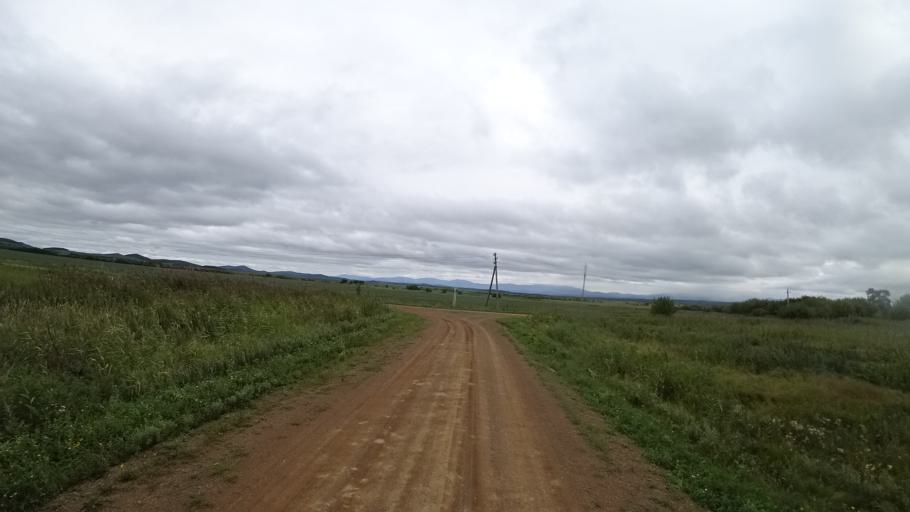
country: RU
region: Primorskiy
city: Chernigovka
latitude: 44.4351
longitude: 132.5916
